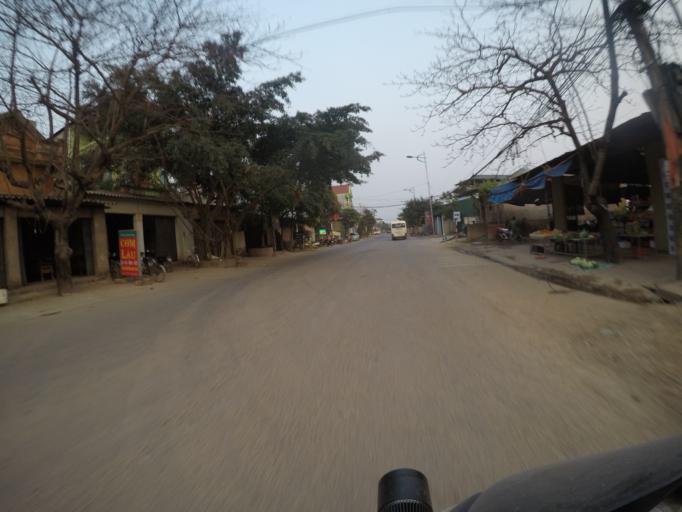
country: VN
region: Vinh Phuc
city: Trai Ngau
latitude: 21.4260
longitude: 105.5930
